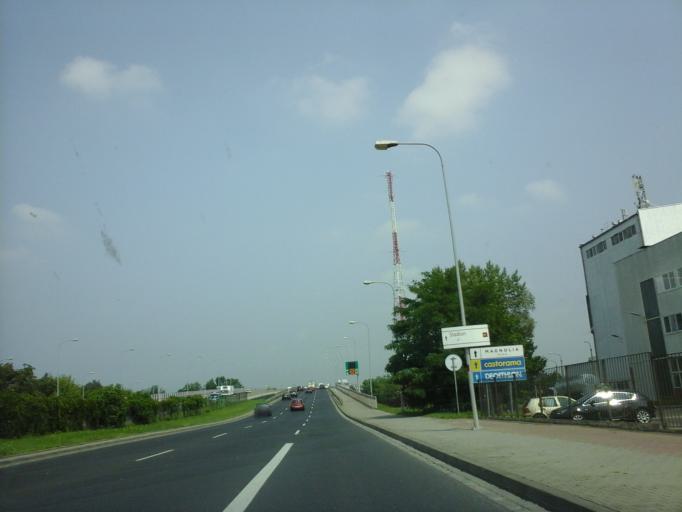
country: PL
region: Lower Silesian Voivodeship
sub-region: Powiat wroclawski
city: Wroclaw
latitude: 51.1120
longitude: 16.9687
